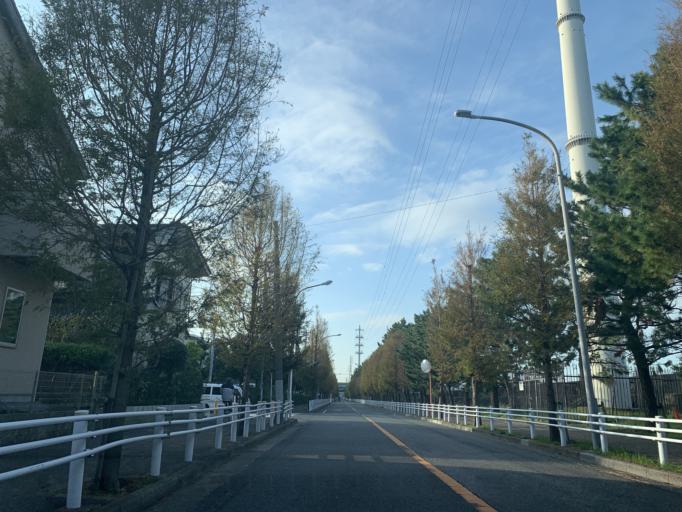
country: JP
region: Tokyo
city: Urayasu
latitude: 35.6531
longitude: 139.9214
